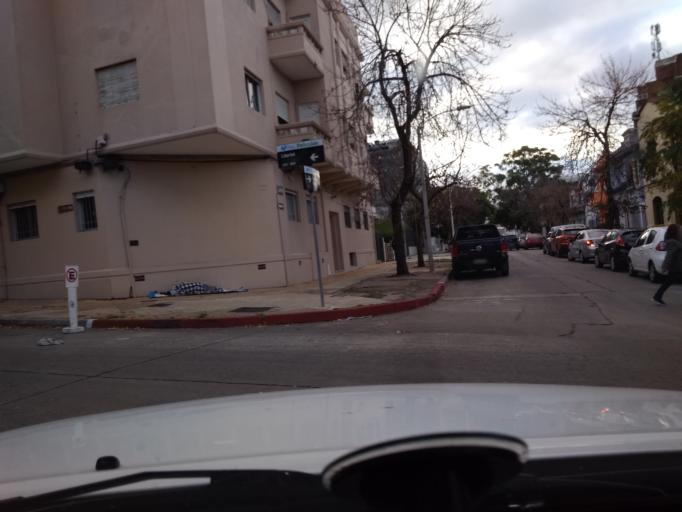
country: UY
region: Montevideo
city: Montevideo
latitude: -34.9078
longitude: -56.1523
